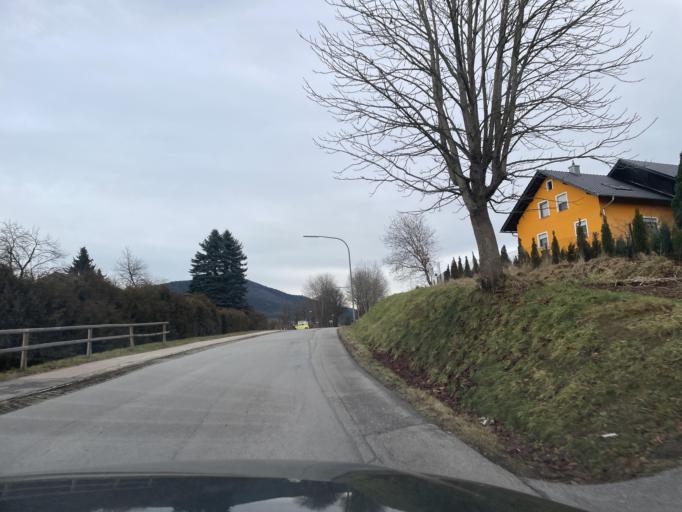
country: DE
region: Bavaria
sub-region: Upper Palatinate
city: Kotzting
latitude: 49.1761
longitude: 12.8721
